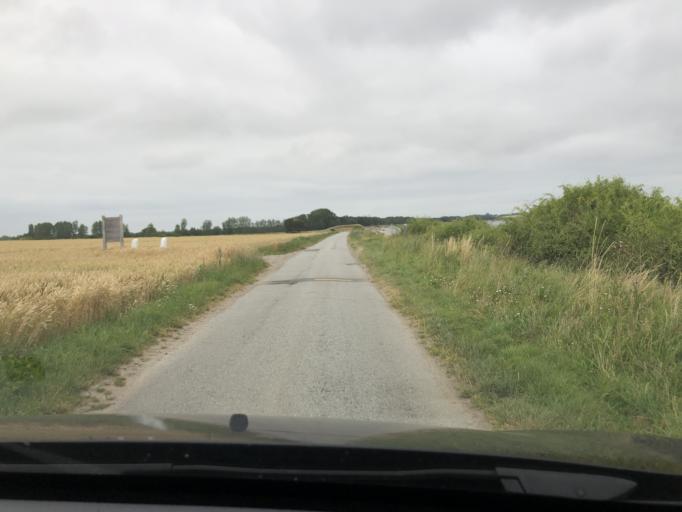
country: DK
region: South Denmark
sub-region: AEro Kommune
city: AEroskobing
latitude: 54.8334
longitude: 10.4416
